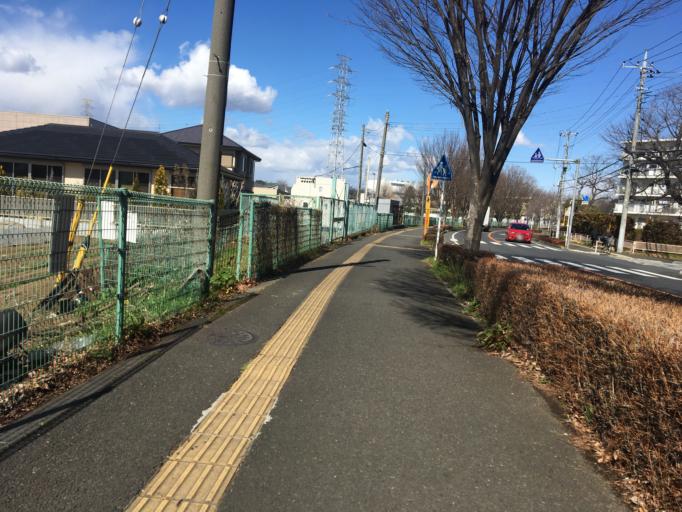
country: JP
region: Saitama
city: Shiki
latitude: 35.8171
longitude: 139.5559
